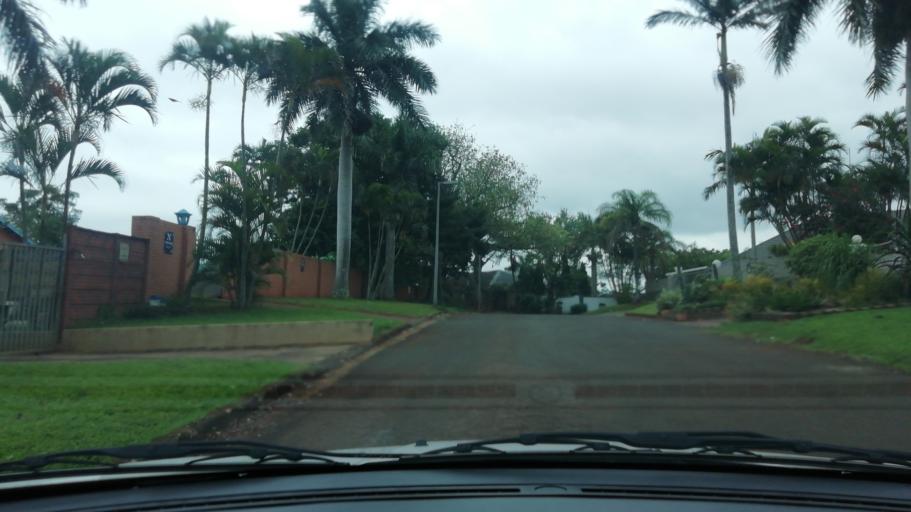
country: ZA
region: KwaZulu-Natal
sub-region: uThungulu District Municipality
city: Empangeni
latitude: -28.7651
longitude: 31.8966
